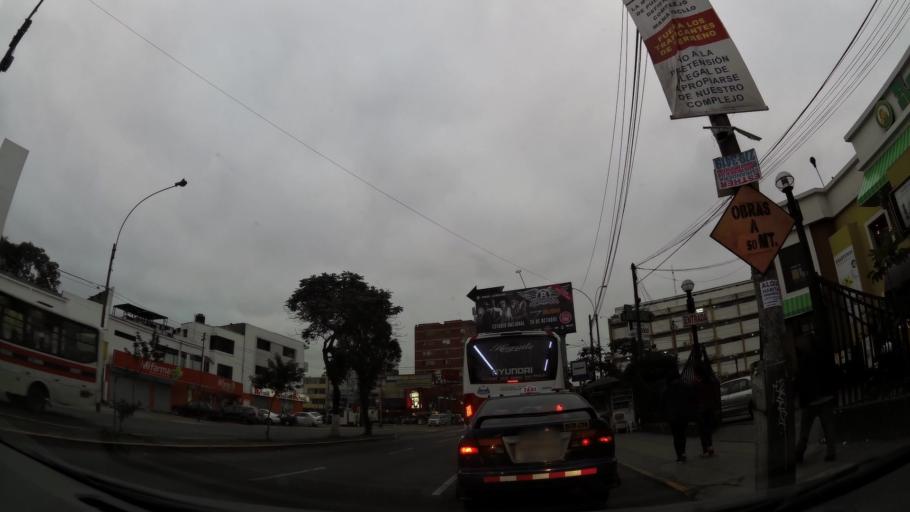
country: PE
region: Lima
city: Lima
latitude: -12.0718
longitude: -77.0621
